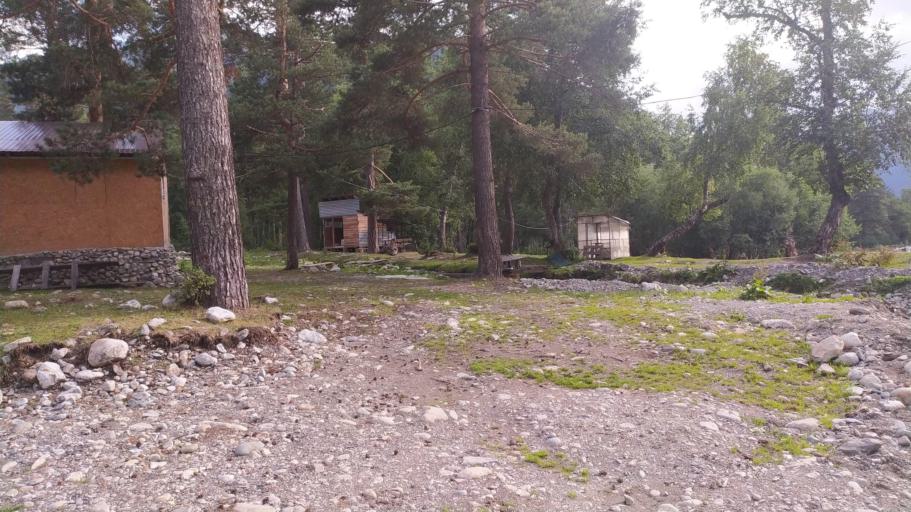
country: RU
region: Karachayevo-Cherkesiya
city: Nizhniy Arkhyz
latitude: 43.5139
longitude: 41.2267
